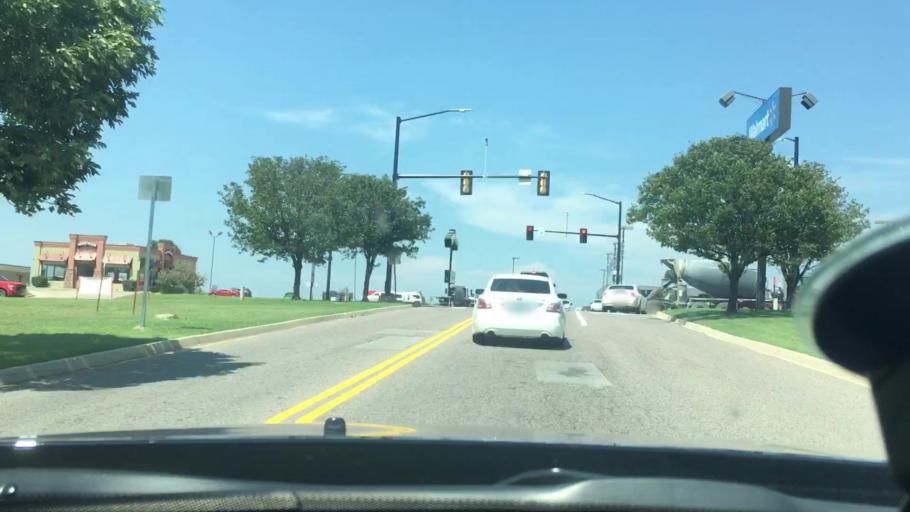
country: US
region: Oklahoma
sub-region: Pontotoc County
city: Ada
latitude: 34.7900
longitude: -96.6555
